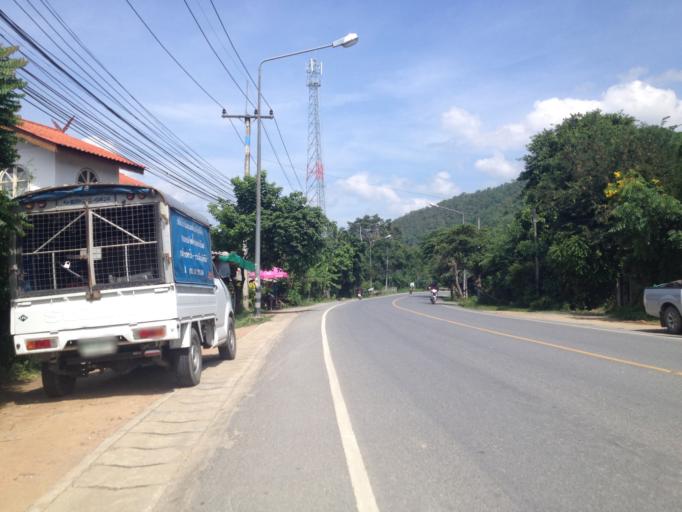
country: TH
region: Chiang Mai
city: Hang Dong
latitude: 18.7327
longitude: 98.9056
